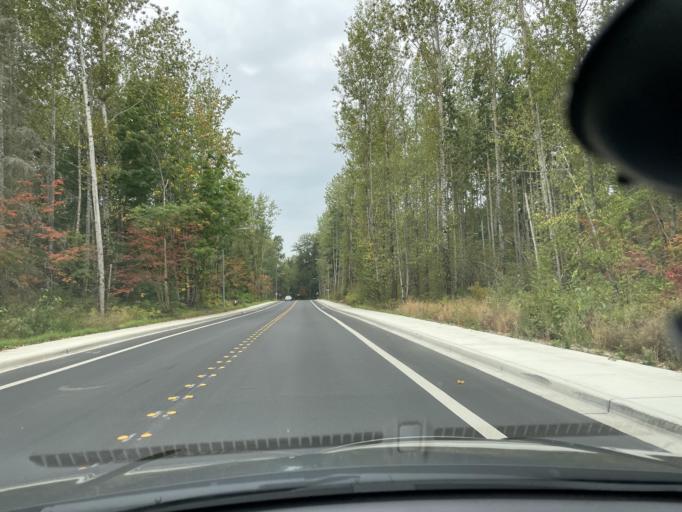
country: US
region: Washington
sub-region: Whatcom County
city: Bellingham
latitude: 48.8042
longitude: -122.5049
